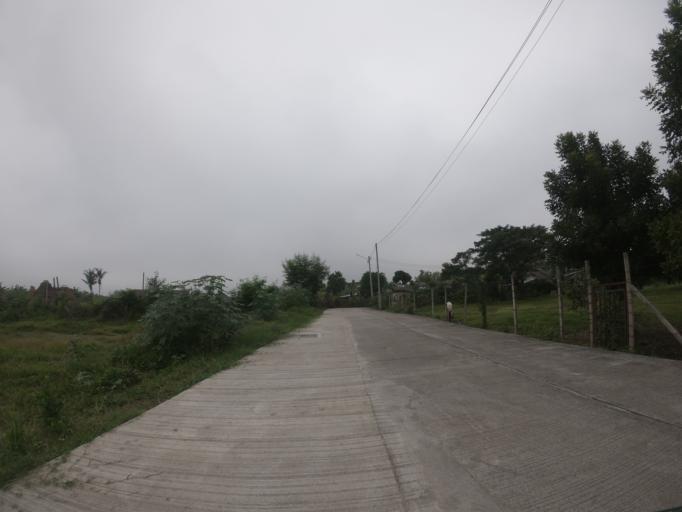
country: TH
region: Chiang Mai
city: Hang Dong
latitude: 18.7410
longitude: 98.9468
